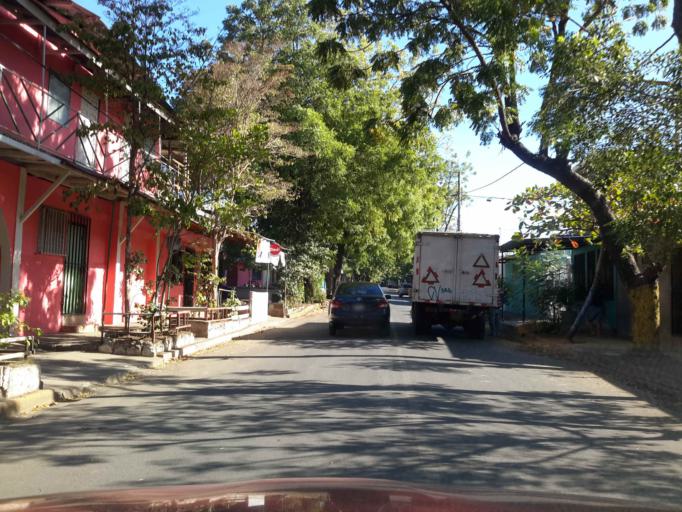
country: NI
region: Managua
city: Managua
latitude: 12.1303
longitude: -86.2739
